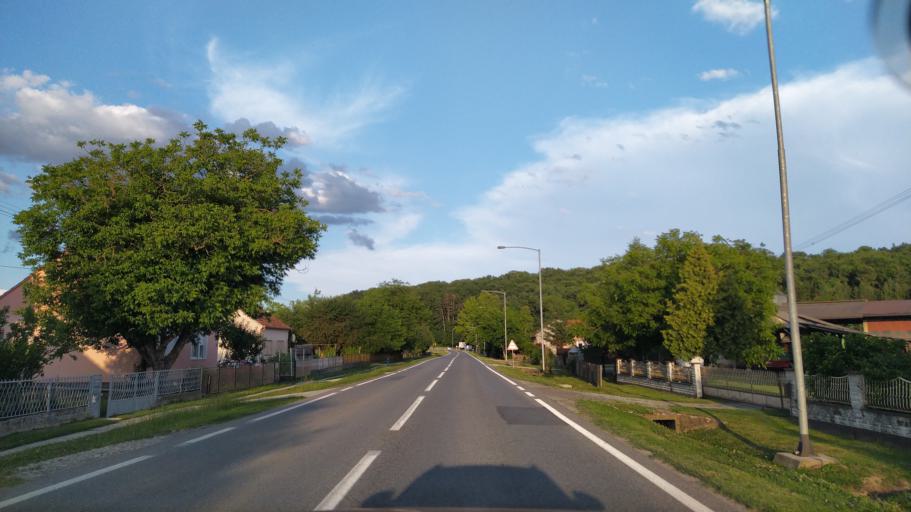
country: HR
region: Osjecko-Baranjska
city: Martin
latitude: 45.4915
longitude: 18.0250
